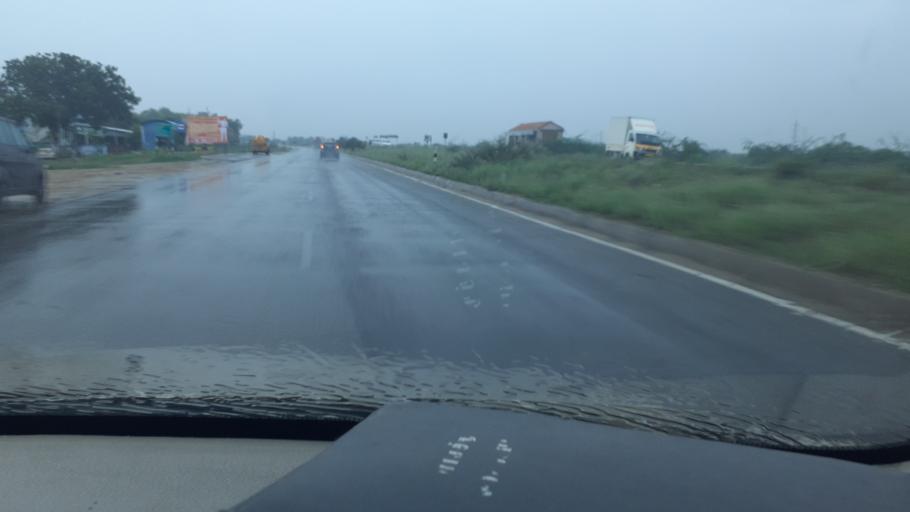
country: IN
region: Tamil Nadu
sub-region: Virudhunagar
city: Sattur
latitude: 9.4173
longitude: 77.9165
